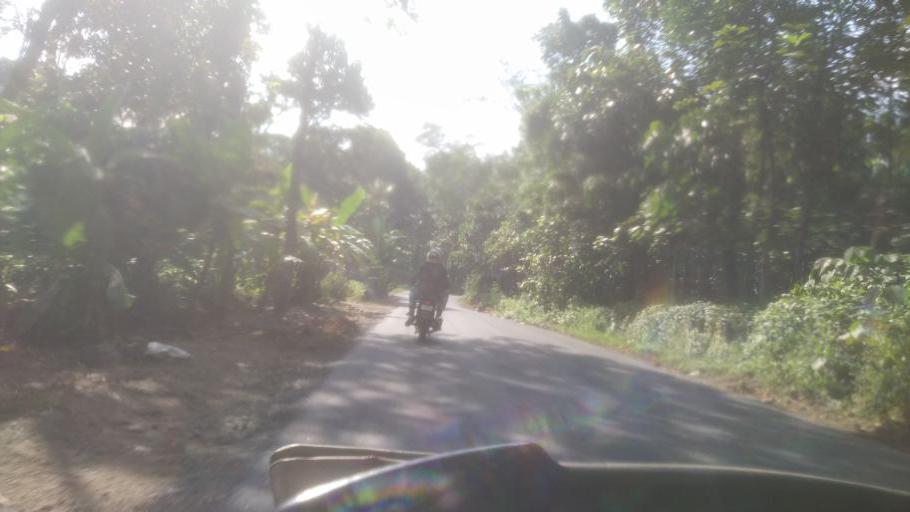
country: IN
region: Kerala
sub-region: Ernakulam
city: Kotamangalam
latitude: 10.0013
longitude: 76.7271
